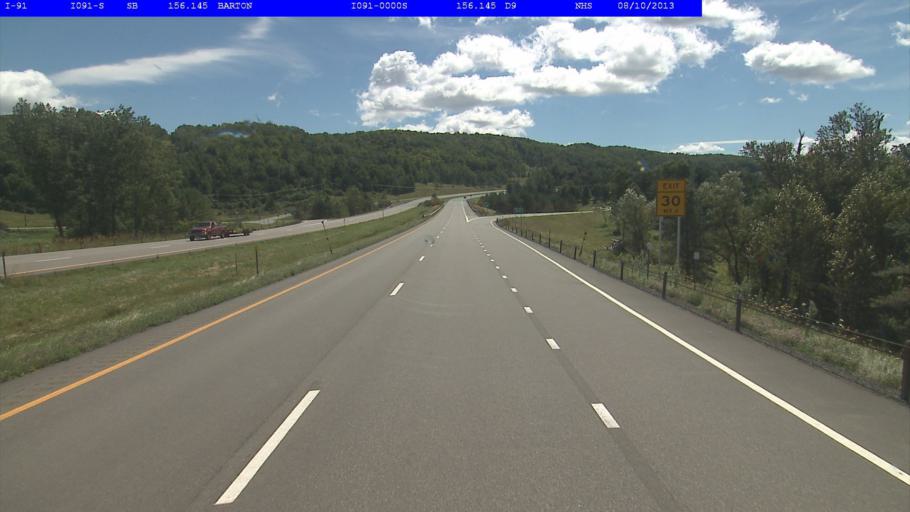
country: US
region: Vermont
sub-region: Orleans County
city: Newport
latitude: 44.7371
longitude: -72.1869
